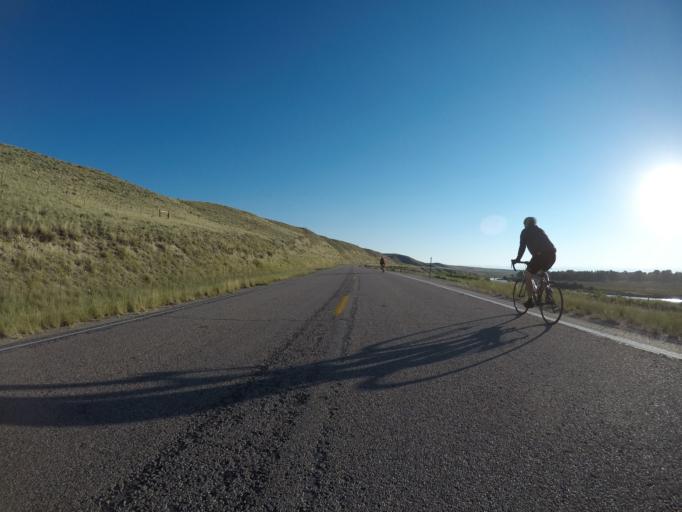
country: US
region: Wyoming
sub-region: Sublette County
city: Marbleton
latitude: 42.5813
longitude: -109.9236
